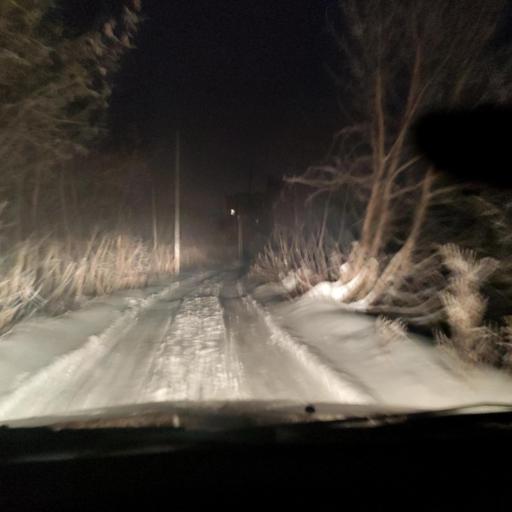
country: RU
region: Bashkortostan
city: Ufa
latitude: 54.7992
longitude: 56.0346
